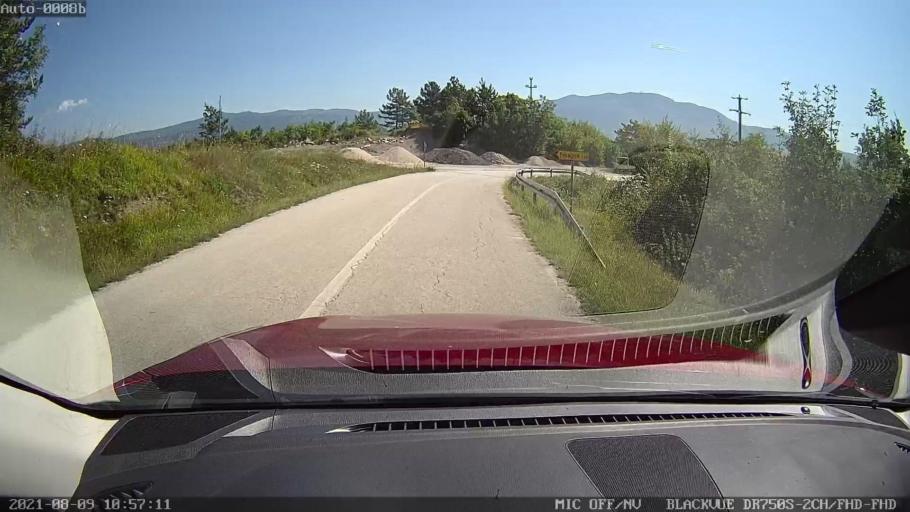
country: HR
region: Istarska
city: Pazin
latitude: 45.2918
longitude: 14.0883
